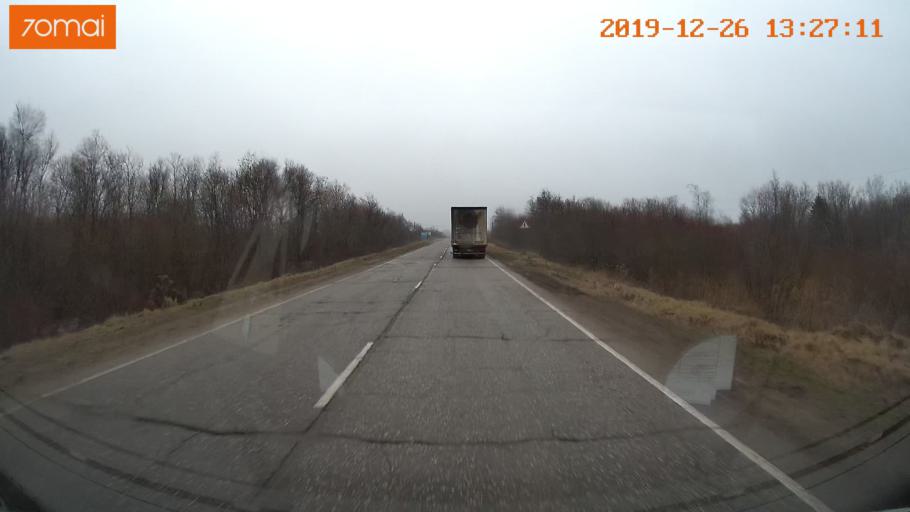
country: RU
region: Vologda
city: Cherepovets
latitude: 58.8553
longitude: 38.2377
